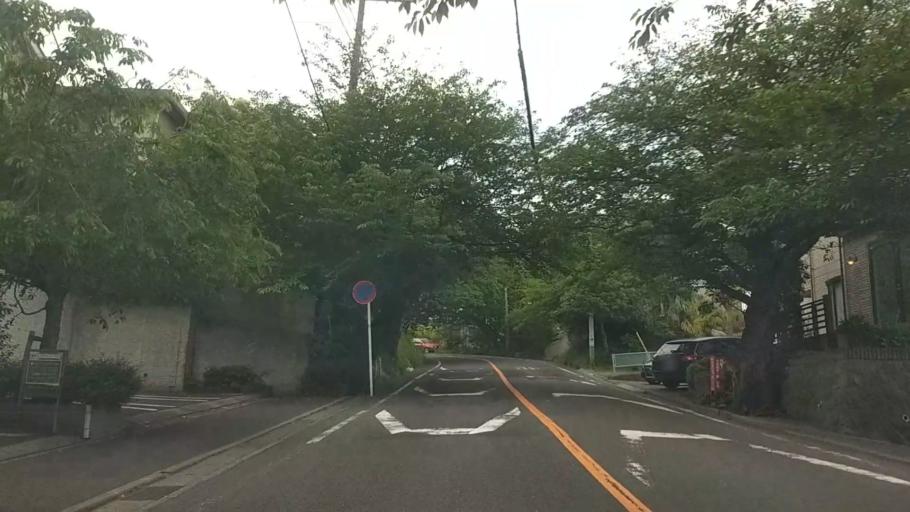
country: JP
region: Kanagawa
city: Kamakura
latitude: 35.3222
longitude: 139.5128
